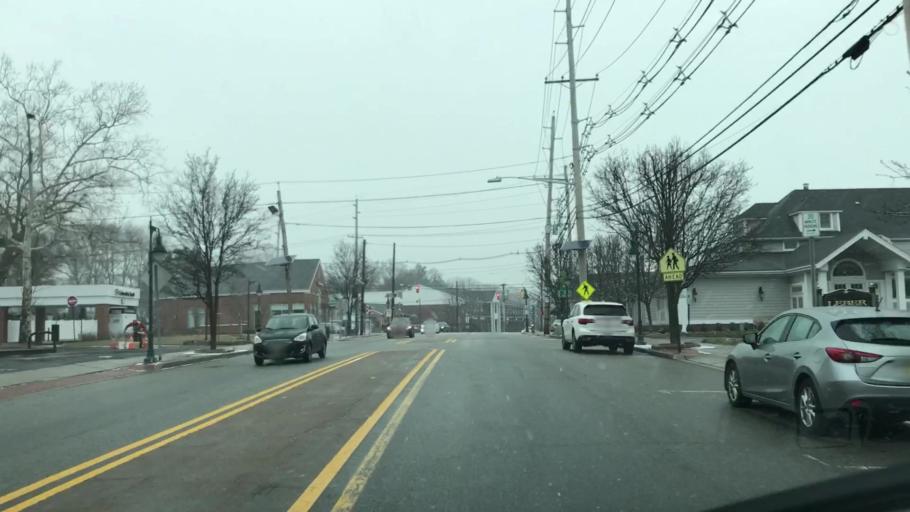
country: US
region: New Jersey
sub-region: Bergen County
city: Oradell
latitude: 40.9489
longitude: -74.0321
